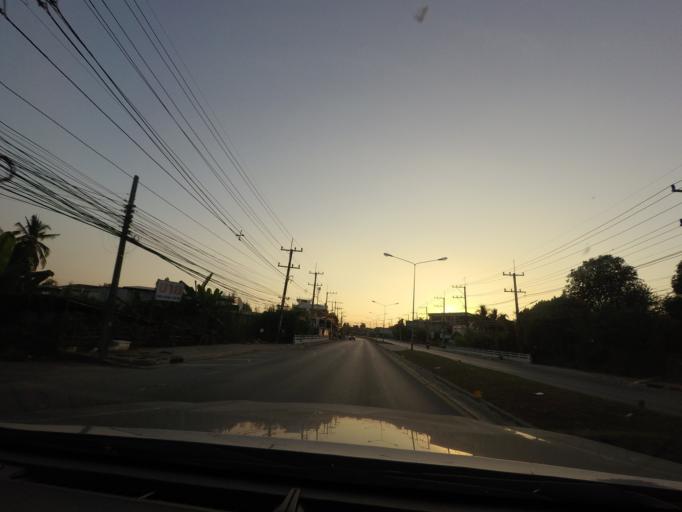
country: TH
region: Sukhothai
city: Sukhothai
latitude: 17.0282
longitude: 99.8242
